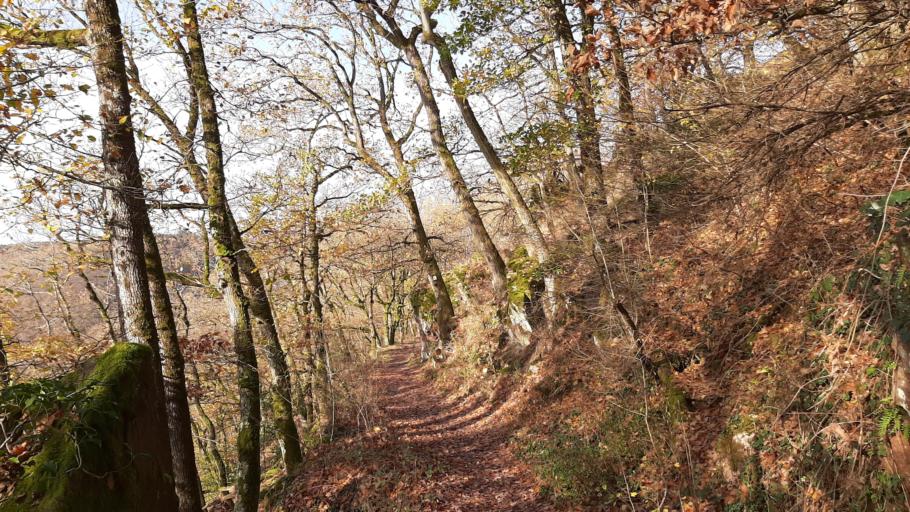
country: DE
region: Saarland
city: Orscholz
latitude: 49.4968
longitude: 6.5535
